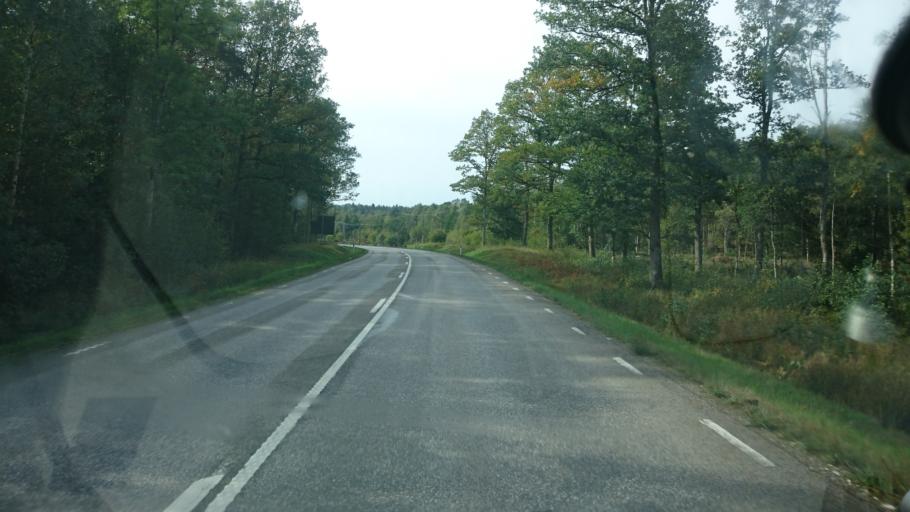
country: SE
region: Vaestra Goetaland
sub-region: Alingsas Kommun
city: Sollebrunn
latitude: 58.0618
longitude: 12.4696
